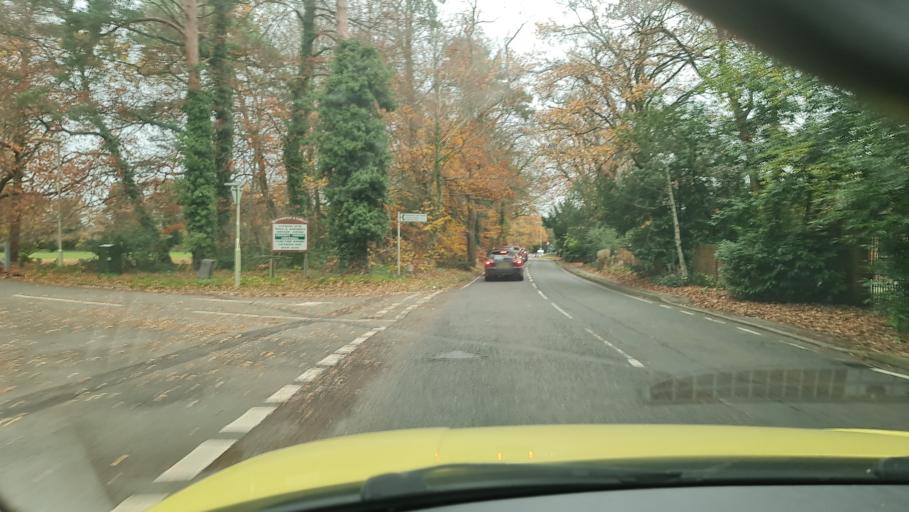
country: GB
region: England
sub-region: Bracknell Forest
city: Sandhurst
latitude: 51.3259
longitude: -0.7791
